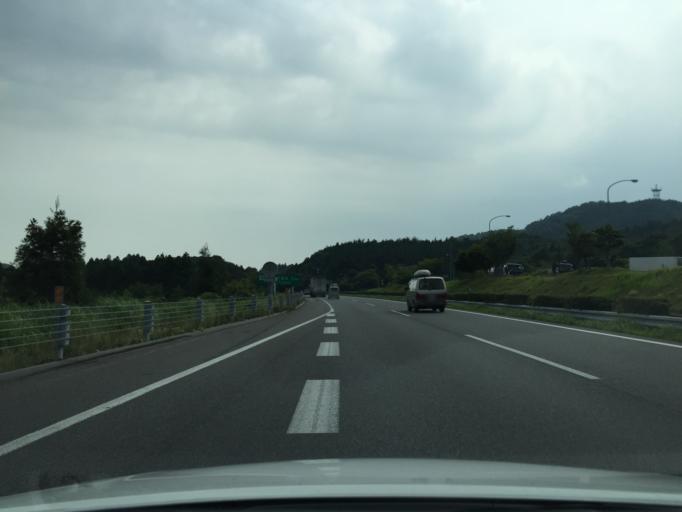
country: JP
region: Fukushima
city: Iwaki
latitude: 37.0208
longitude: 140.8133
